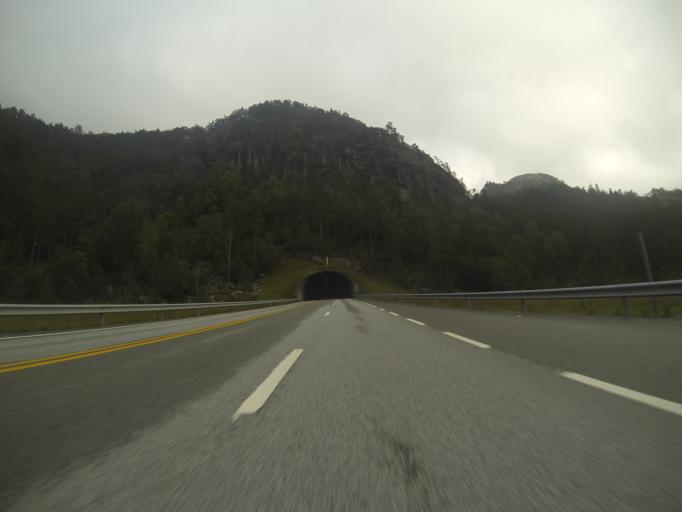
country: NO
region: Hordaland
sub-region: Odda
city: Odda
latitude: 59.8800
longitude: 6.4421
